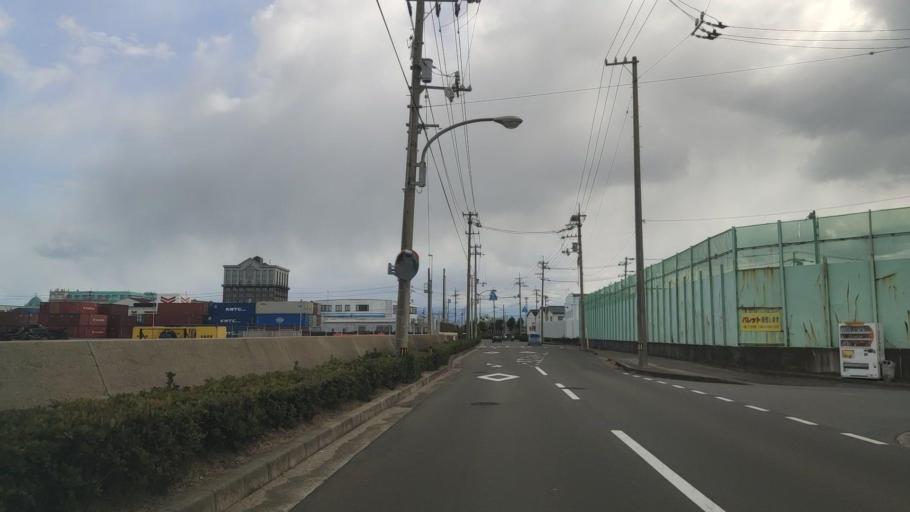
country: JP
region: Ehime
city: Saijo
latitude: 34.0506
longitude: 133.0245
